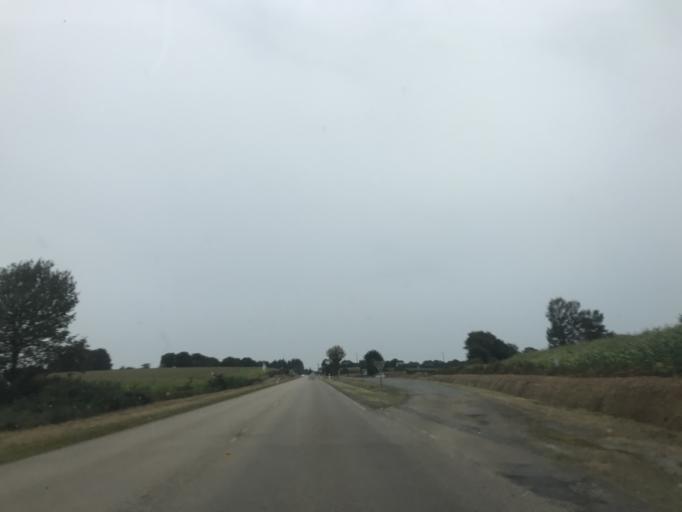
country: FR
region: Brittany
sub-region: Departement du Finistere
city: Plouneour-Menez
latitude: 48.4566
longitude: -3.8775
